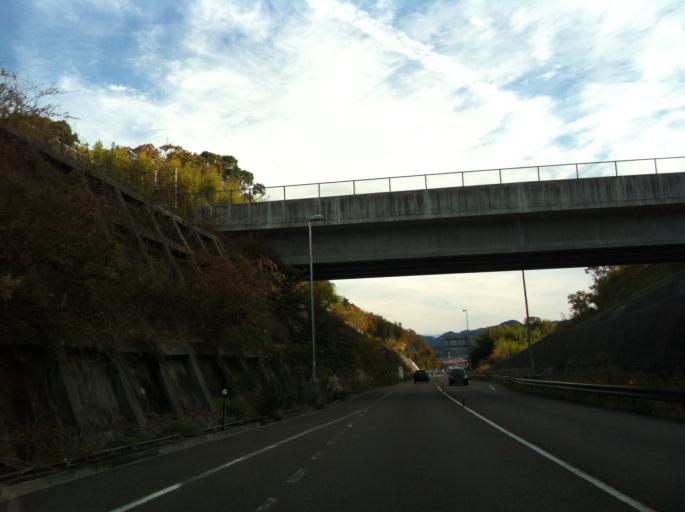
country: JP
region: Gifu
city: Minokamo
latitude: 35.4828
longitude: 137.0494
